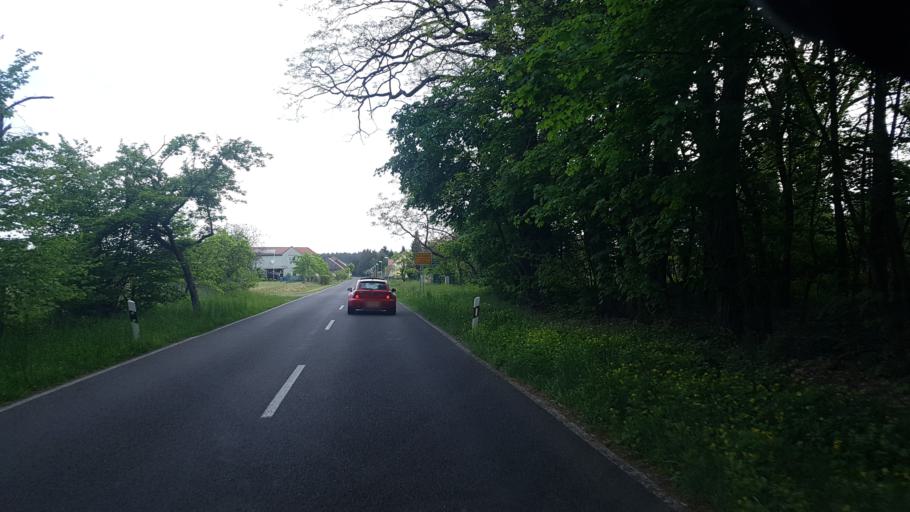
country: DE
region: Brandenburg
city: Baruth
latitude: 51.9856
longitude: 13.4800
